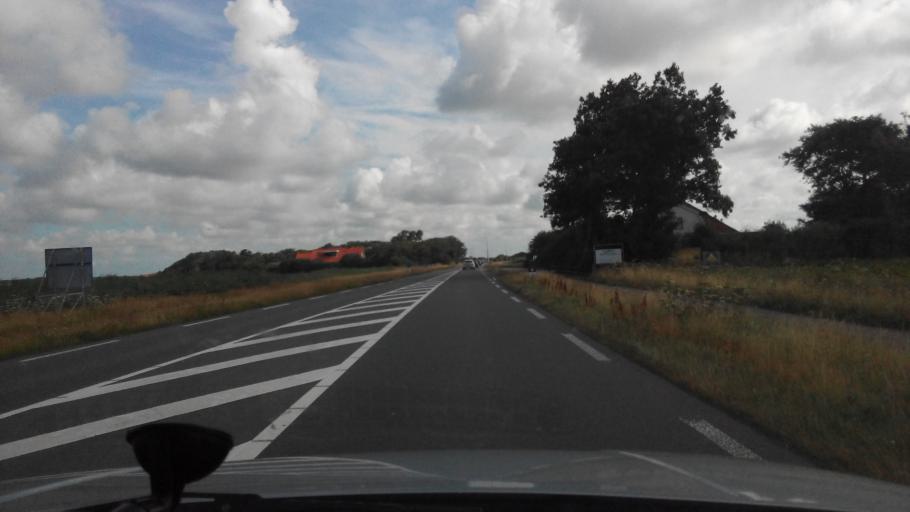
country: NL
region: North Holland
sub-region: Gemeente Texel
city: Den Burg
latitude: 53.0115
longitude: 4.7794
